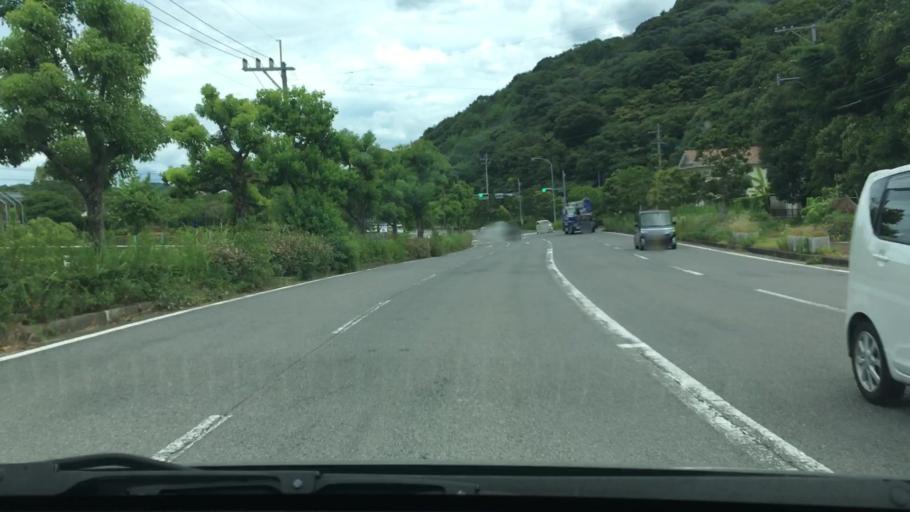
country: JP
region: Nagasaki
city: Sasebo
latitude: 32.9937
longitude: 129.7596
